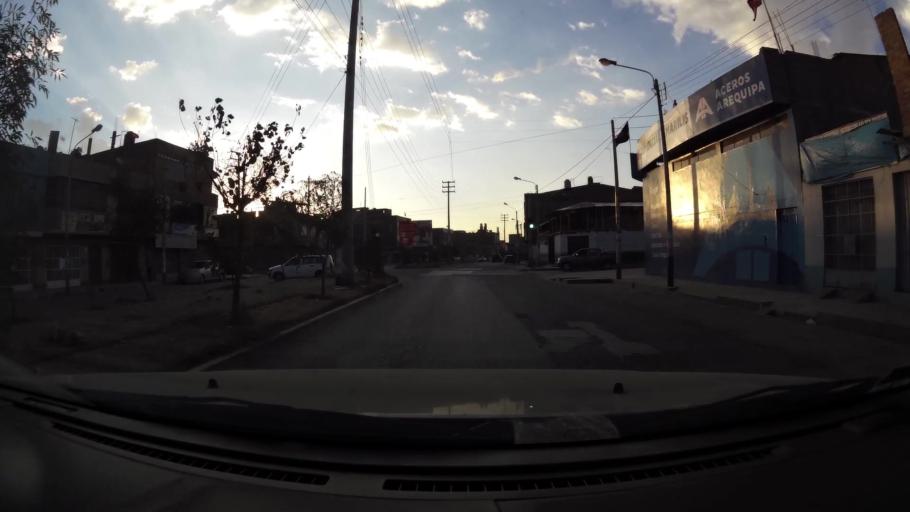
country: PE
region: Junin
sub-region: Provincia de Huancayo
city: Pilcomay
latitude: -12.0489
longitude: -75.2292
